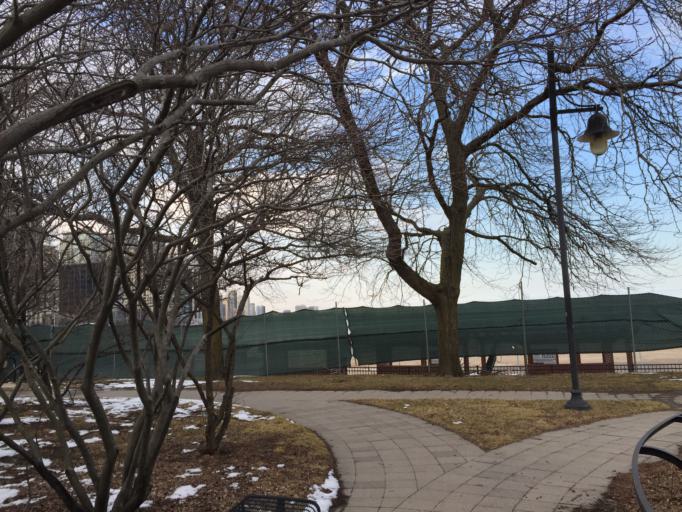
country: US
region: Illinois
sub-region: Cook County
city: Chicago
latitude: 41.8928
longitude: -87.6131
